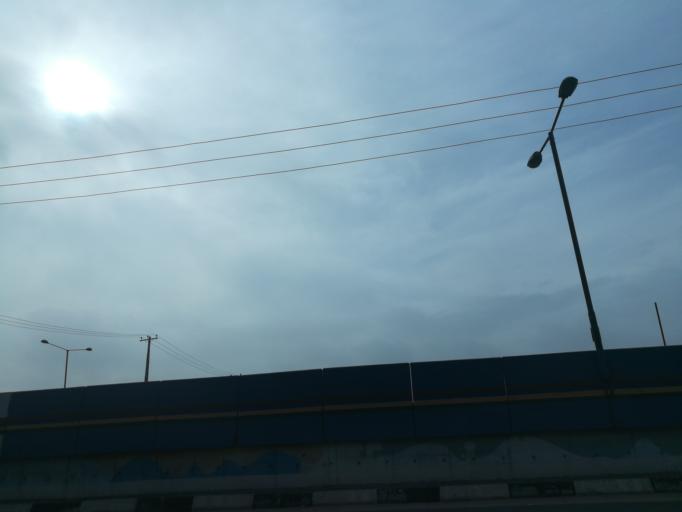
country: NG
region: Lagos
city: Ifako
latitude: 6.6387
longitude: 3.3692
